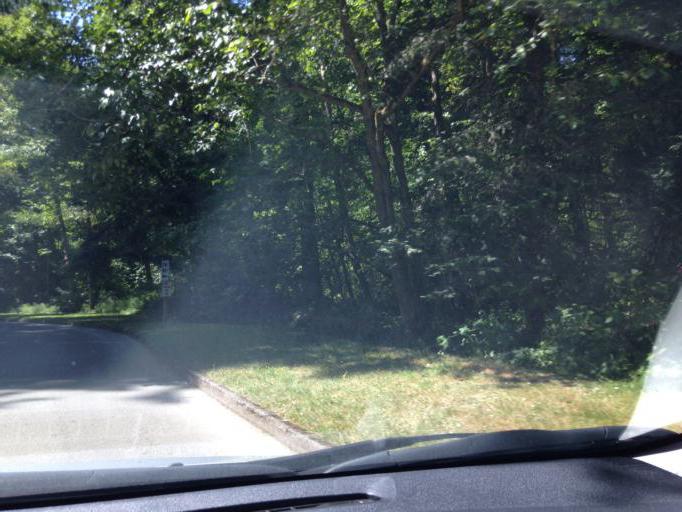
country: US
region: Washington
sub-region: King County
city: Mercer Island
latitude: 47.5528
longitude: -122.2494
